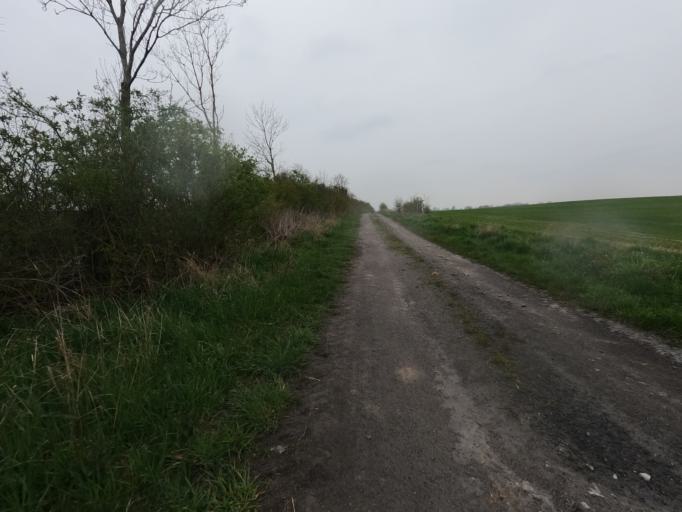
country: PL
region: West Pomeranian Voivodeship
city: Trzcinsko Zdroj
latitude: 52.9205
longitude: 14.7328
